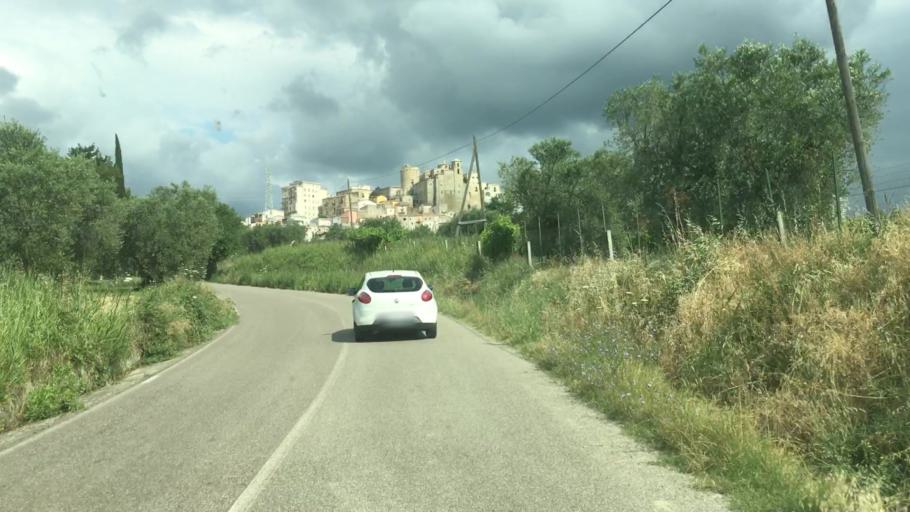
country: IT
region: Basilicate
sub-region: Provincia di Matera
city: San Mauro Forte
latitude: 40.4828
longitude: 16.2574
